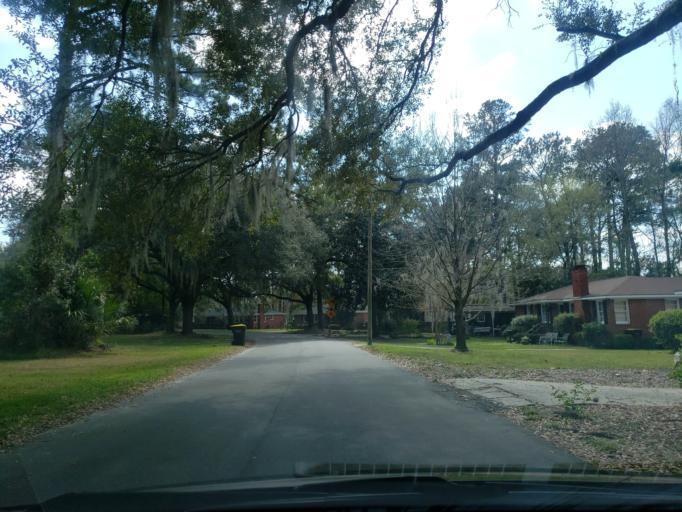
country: US
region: Georgia
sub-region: Chatham County
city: Thunderbolt
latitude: 32.0251
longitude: -81.1072
